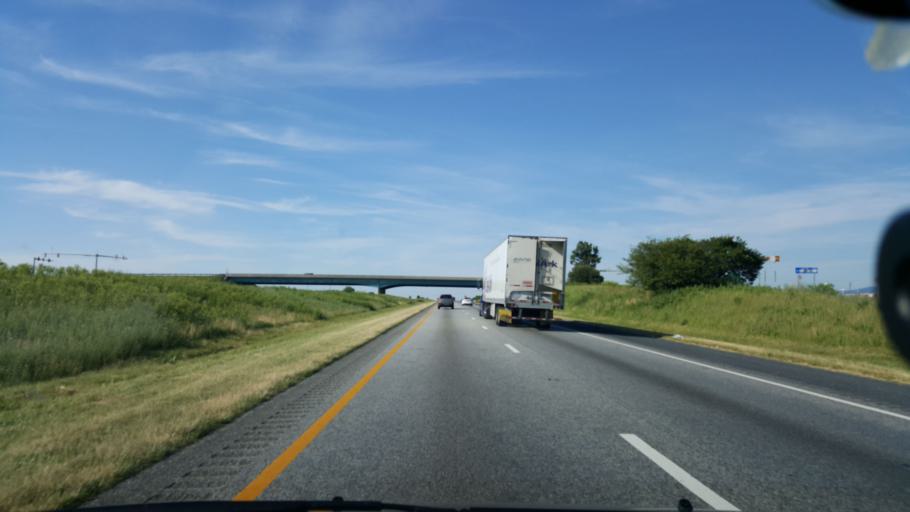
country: US
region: Virginia
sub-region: Rockingham County
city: Bridgewater
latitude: 38.3550
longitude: -78.9283
